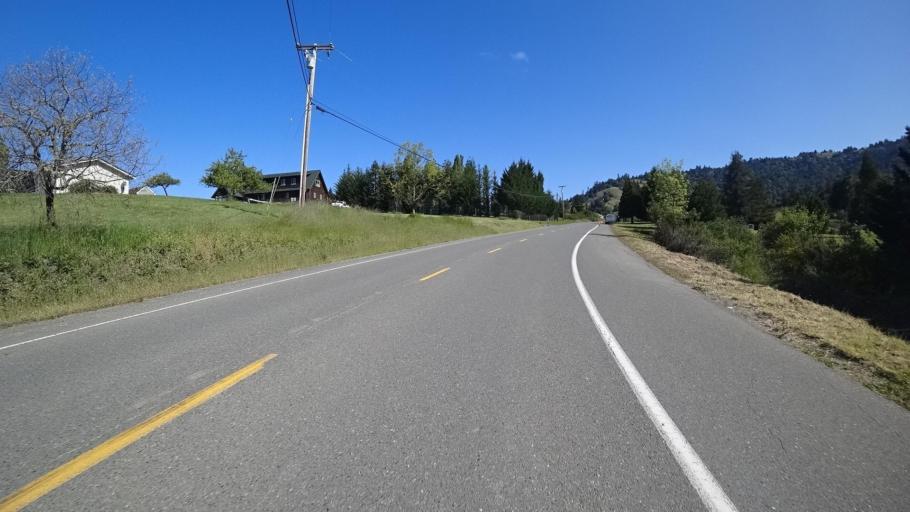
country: US
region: California
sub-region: Humboldt County
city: Redway
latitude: 40.1085
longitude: -123.7855
